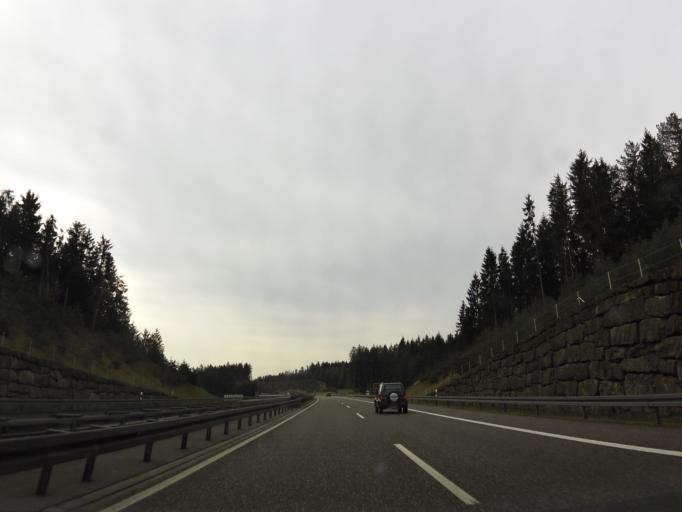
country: DE
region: Thuringia
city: Sankt Kilian
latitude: 50.5354
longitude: 10.7415
